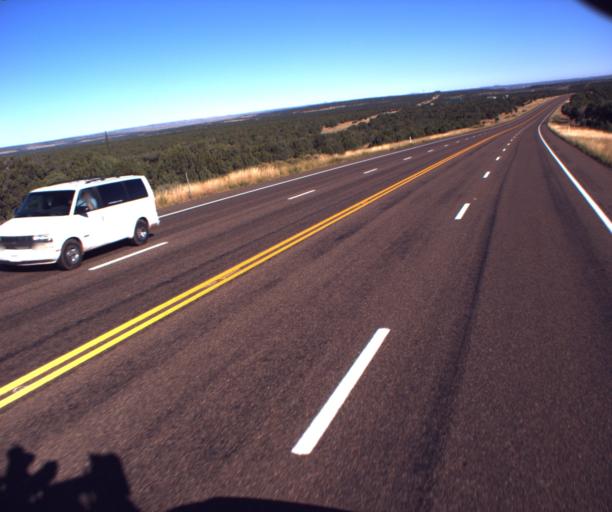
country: US
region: Arizona
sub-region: Navajo County
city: White Mountain Lake
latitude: 34.3448
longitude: -110.0521
